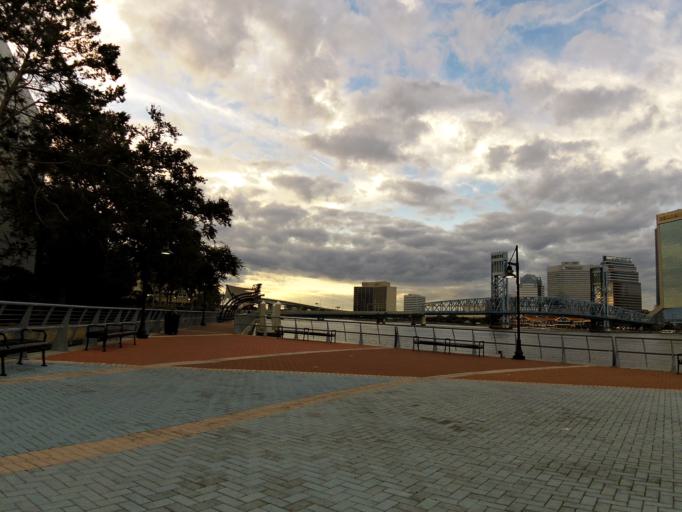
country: US
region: Florida
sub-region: Duval County
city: Jacksonville
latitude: 30.3199
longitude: -81.6556
